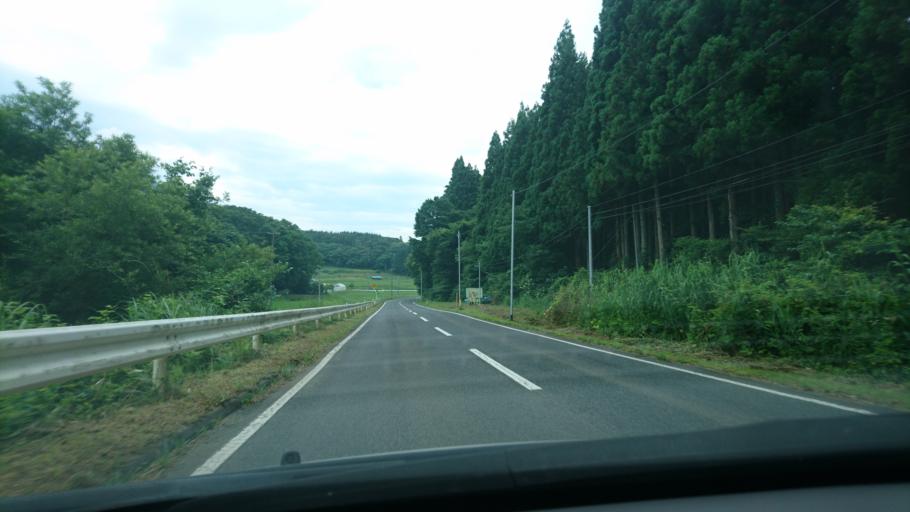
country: JP
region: Iwate
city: Ichinoseki
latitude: 38.8808
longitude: 141.4258
